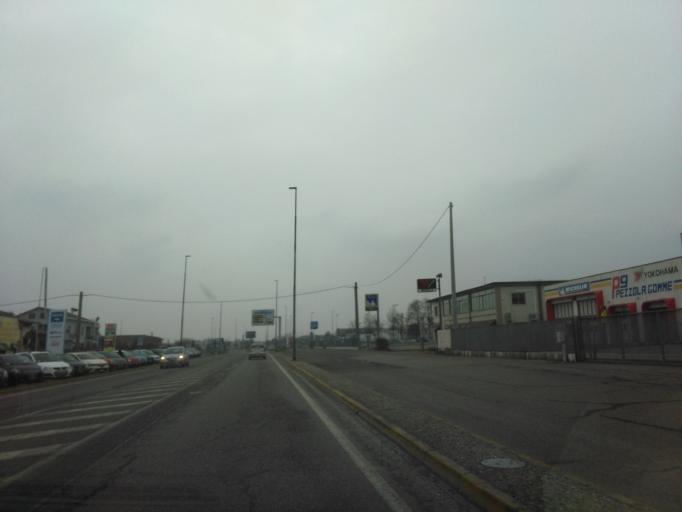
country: IT
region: Lombardy
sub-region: Provincia di Brescia
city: Orzinuovi
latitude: 45.4099
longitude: 9.9342
